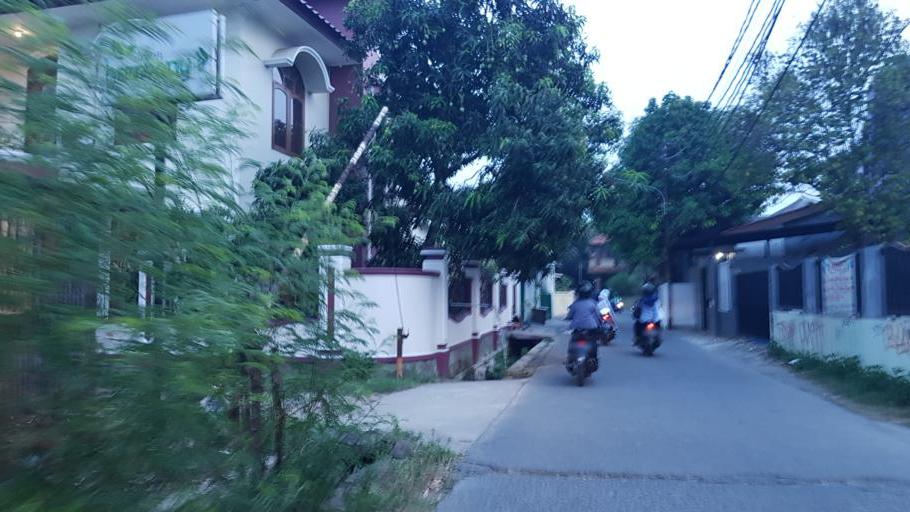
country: ID
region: West Java
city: Pamulang
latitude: -6.3263
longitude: 106.7932
